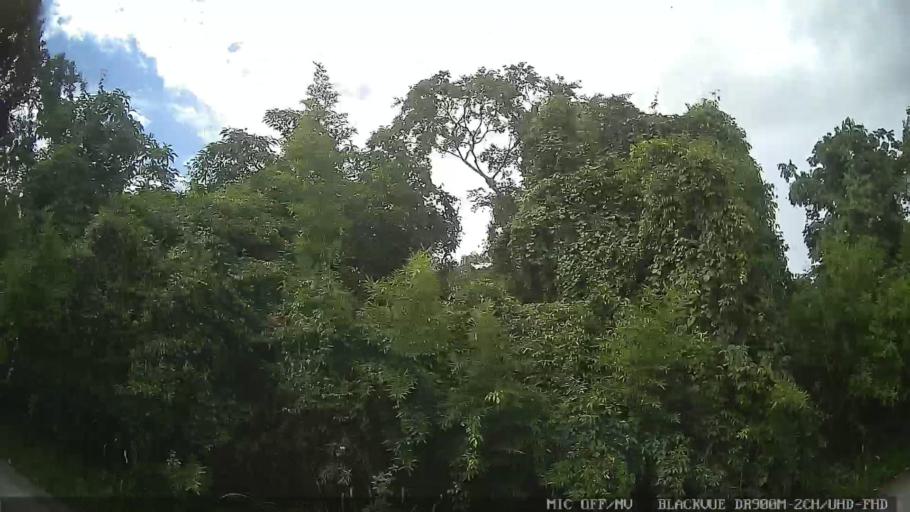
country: BR
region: Sao Paulo
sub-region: Santa Branca
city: Santa Branca
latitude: -23.5238
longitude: -45.8652
